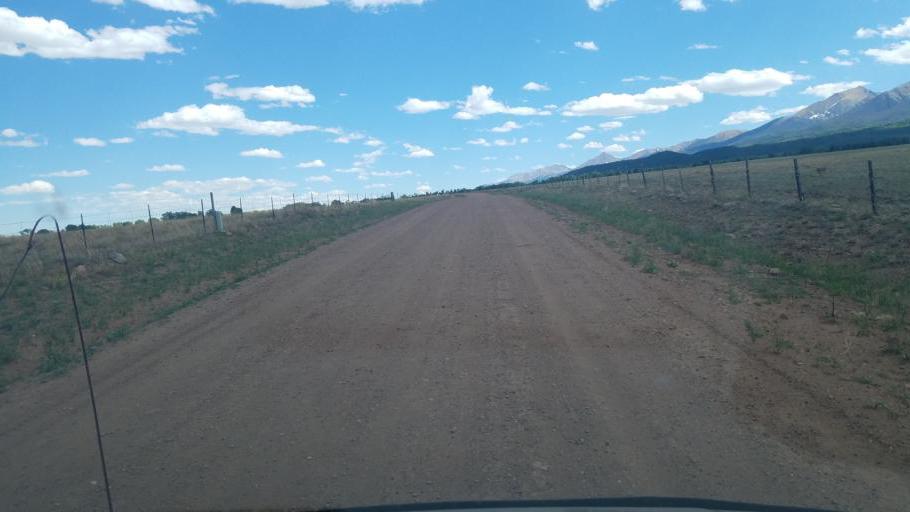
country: US
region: Colorado
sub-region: Custer County
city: Westcliffe
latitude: 38.2471
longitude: -105.6090
